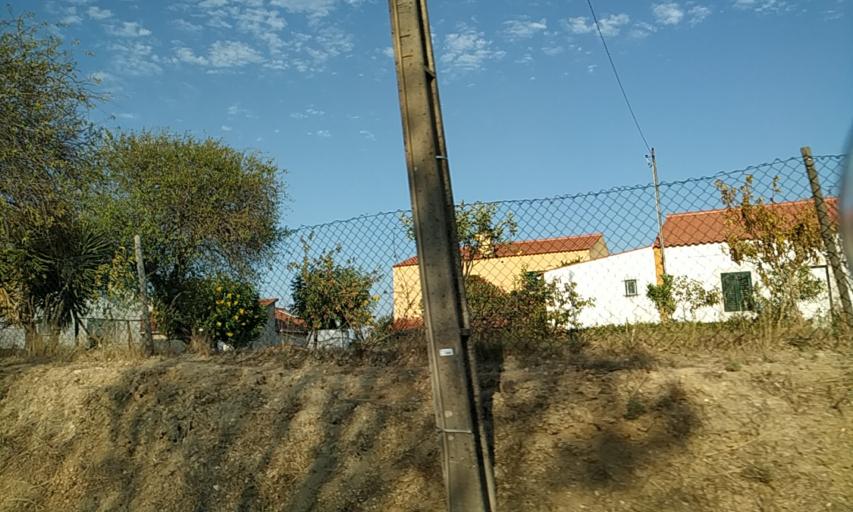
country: PT
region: Santarem
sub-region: Alcanena
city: Alcanena
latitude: 39.4108
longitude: -8.6382
